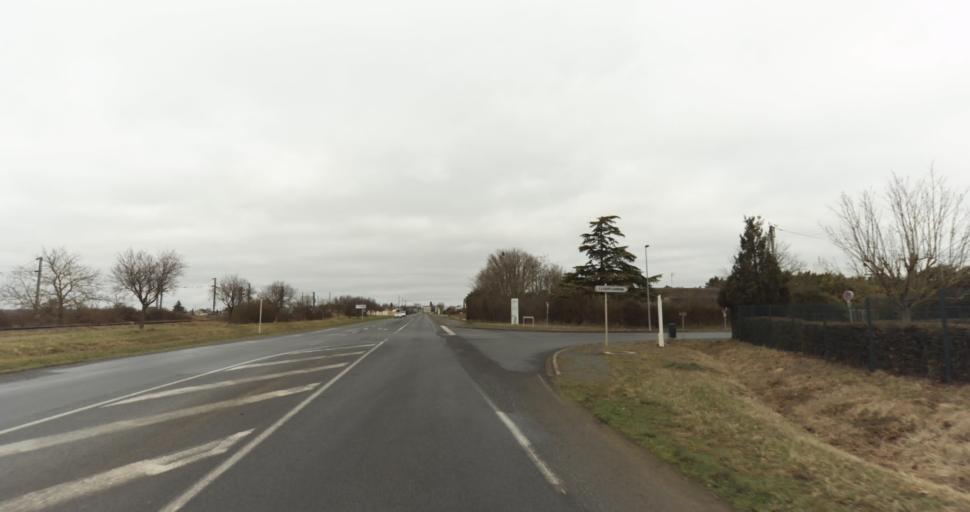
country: FR
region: Pays de la Loire
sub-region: Departement de Maine-et-Loire
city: Montreuil-Bellay
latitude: 47.1209
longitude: -0.1369
